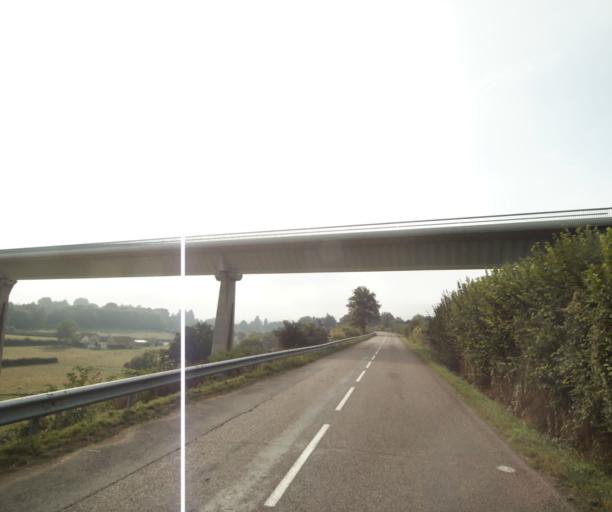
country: FR
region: Bourgogne
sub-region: Departement de Saone-et-Loire
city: Charolles
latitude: 46.4433
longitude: 4.2688
